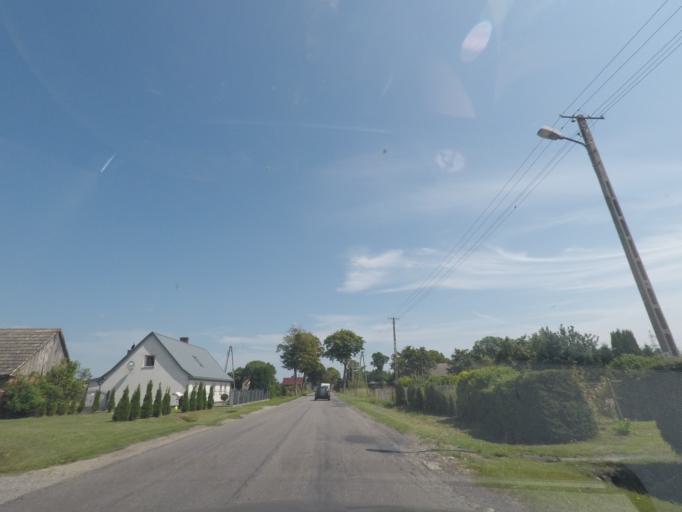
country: PL
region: West Pomeranian Voivodeship
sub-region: Powiat slawienski
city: Darlowo
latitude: 54.4476
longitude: 16.4653
